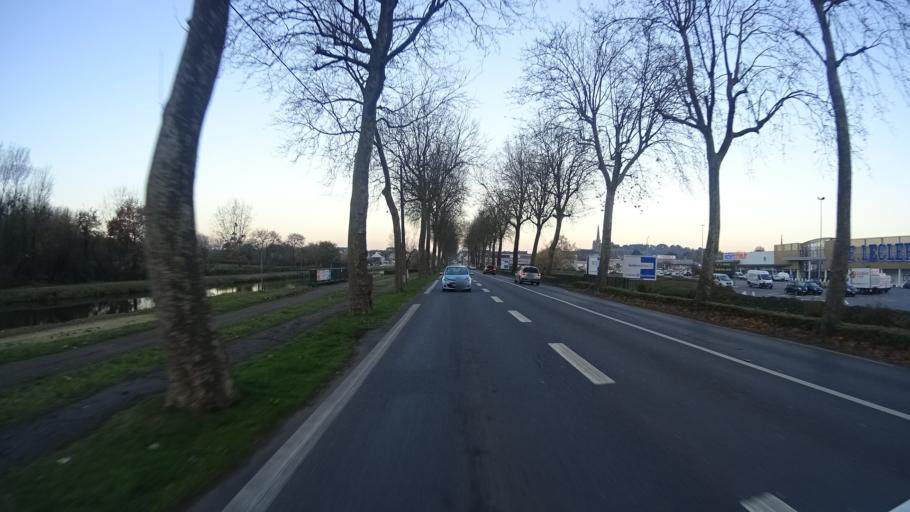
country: FR
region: Brittany
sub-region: Departement d'Ille-et-Vilaine
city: Redon
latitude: 47.6459
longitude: -2.0773
